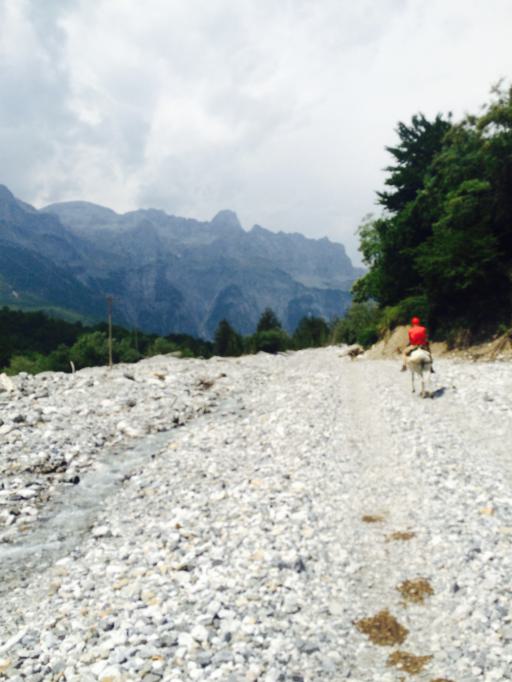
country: AL
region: Shkoder
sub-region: Rrethi i Shkodres
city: Nicaj-Shale
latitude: 42.3981
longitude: 19.7718
